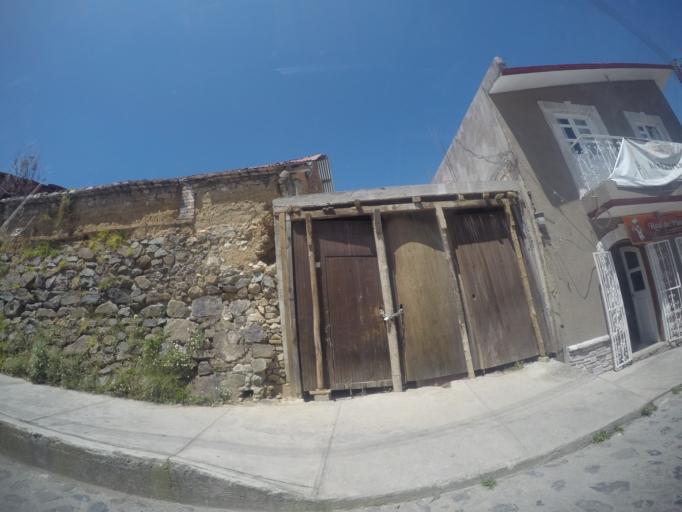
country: MX
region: Hidalgo
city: Mineral del Monte
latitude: 20.1381
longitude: -98.6710
